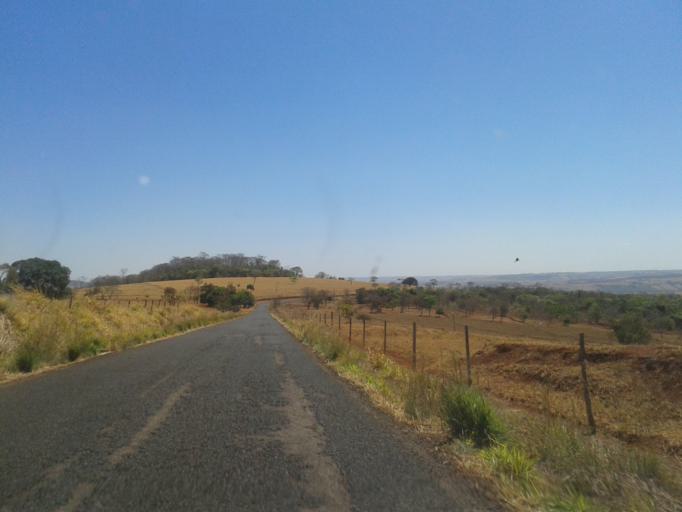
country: BR
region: Minas Gerais
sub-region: Uberlandia
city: Uberlandia
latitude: -18.7928
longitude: -48.2943
